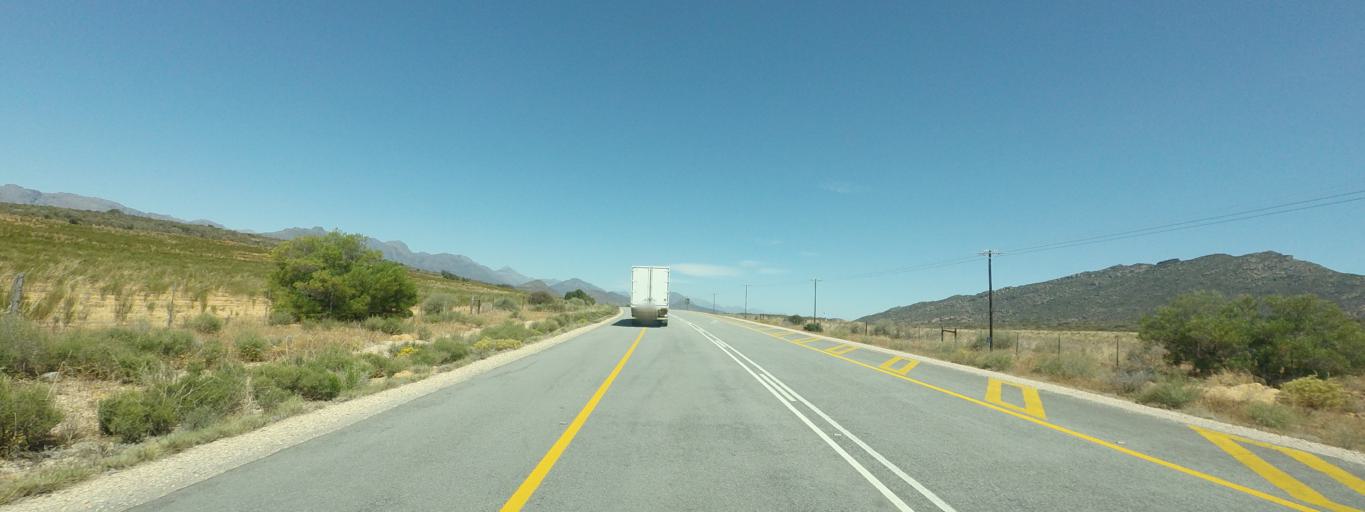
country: ZA
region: Western Cape
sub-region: West Coast District Municipality
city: Clanwilliam
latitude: -32.3188
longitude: 18.9133
